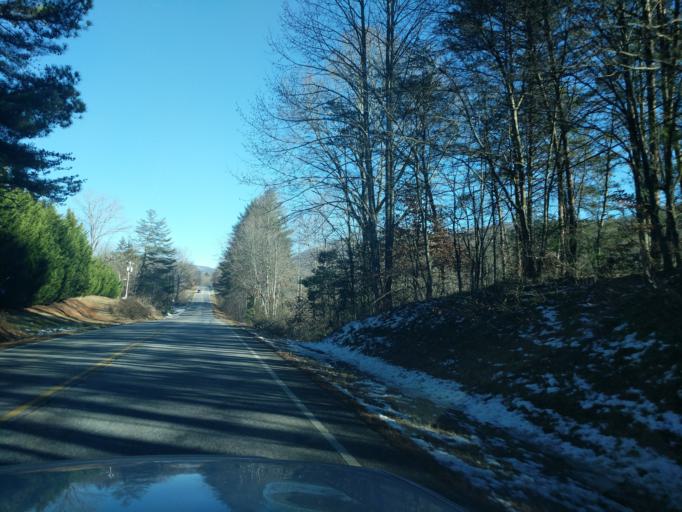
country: US
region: Georgia
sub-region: Towns County
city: Hiawassee
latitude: 34.9254
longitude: -83.6862
